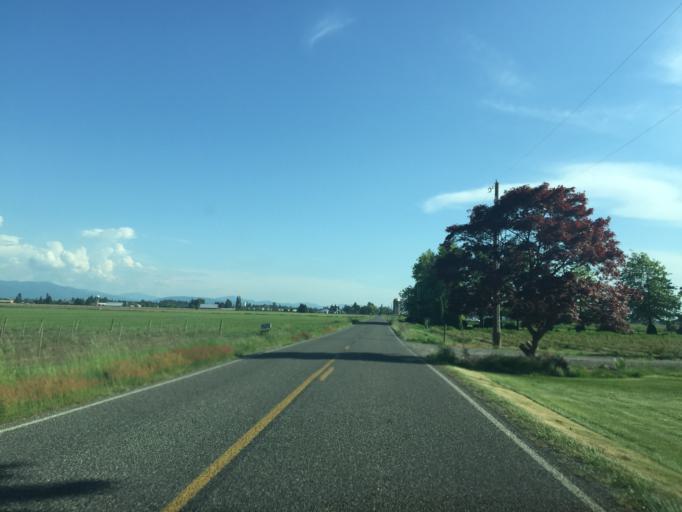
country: US
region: Washington
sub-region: Whatcom County
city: Lynden
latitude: 48.9756
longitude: -122.4628
